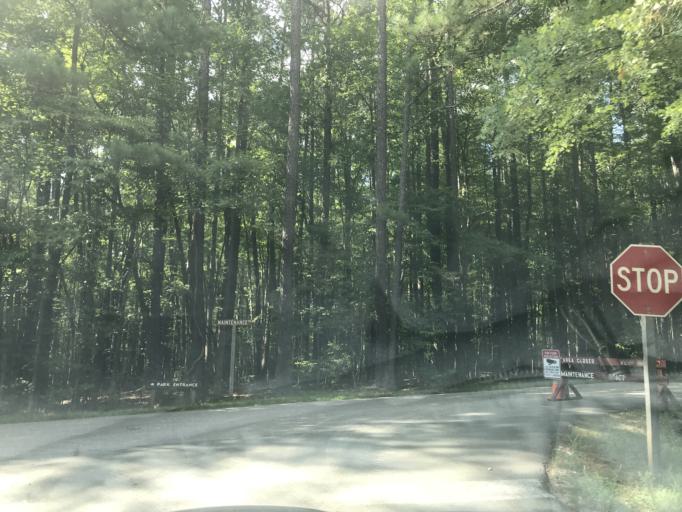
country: US
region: North Carolina
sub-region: Wake County
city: Morrisville
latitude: 35.8781
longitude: -78.7576
